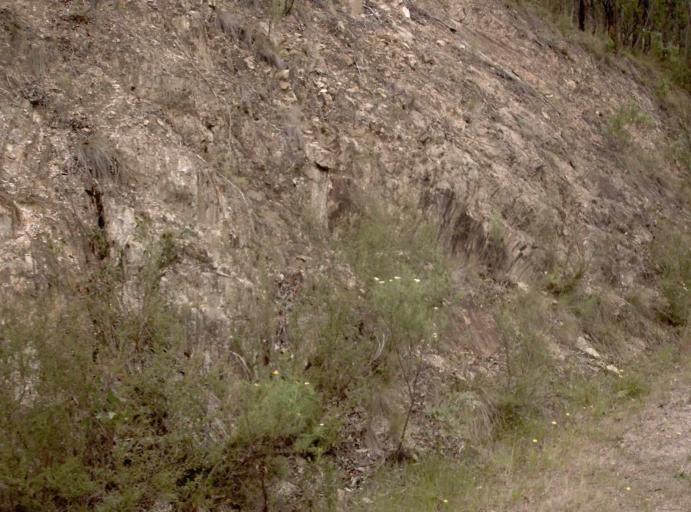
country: AU
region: Victoria
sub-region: East Gippsland
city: Bairnsdale
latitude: -37.6381
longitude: 147.2467
